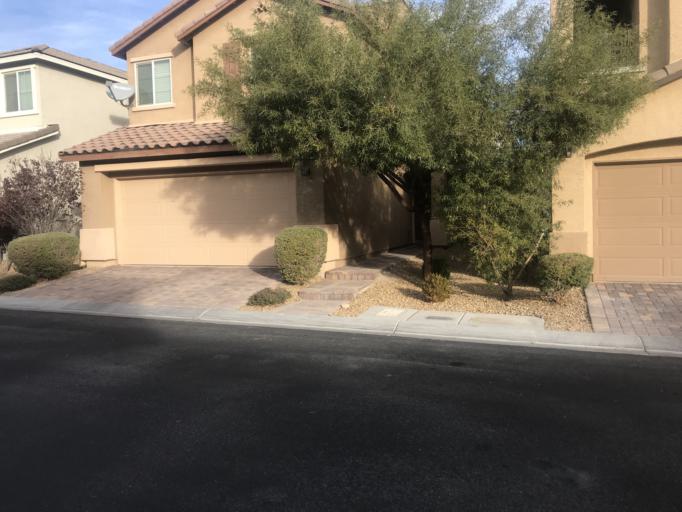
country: US
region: Nevada
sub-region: Clark County
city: Enterprise
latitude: 36.0056
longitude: -115.2879
